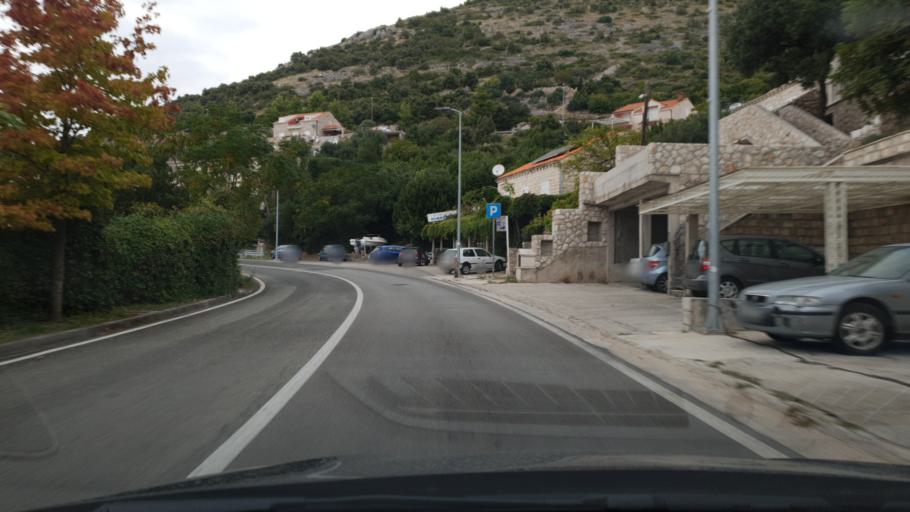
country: HR
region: Dubrovacko-Neretvanska
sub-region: Grad Dubrovnik
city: Mokosica
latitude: 42.6723
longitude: 18.0688
